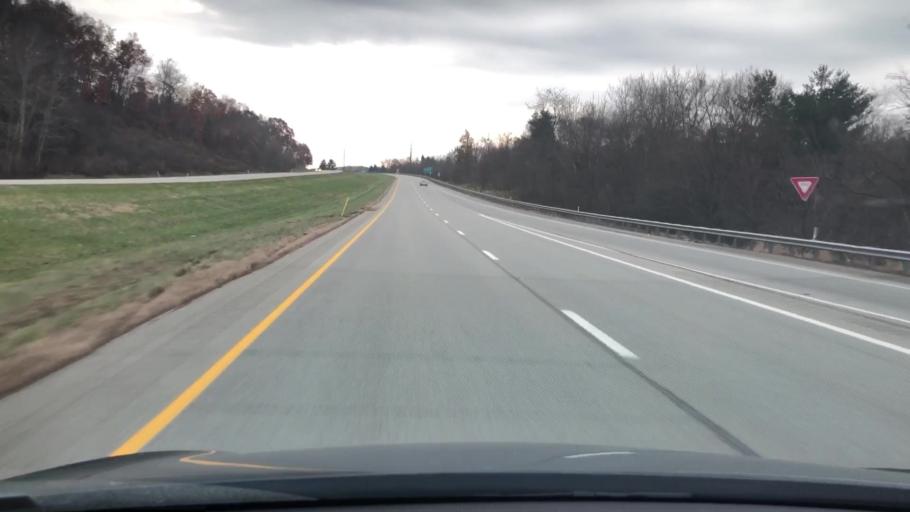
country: US
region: Pennsylvania
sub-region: Armstrong County
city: Freeport
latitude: 40.6870
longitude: -79.7120
